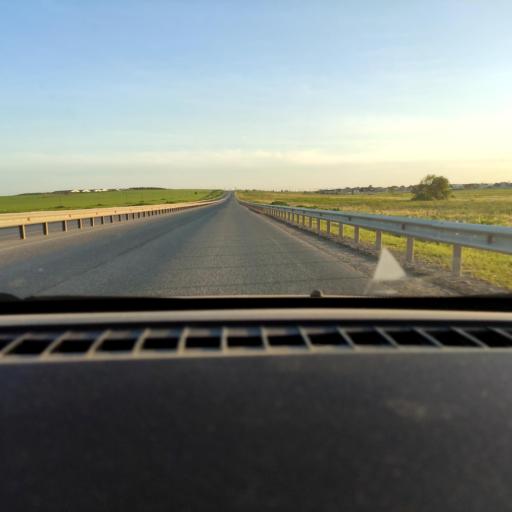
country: RU
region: Perm
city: Kultayevo
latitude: 57.8790
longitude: 55.9102
